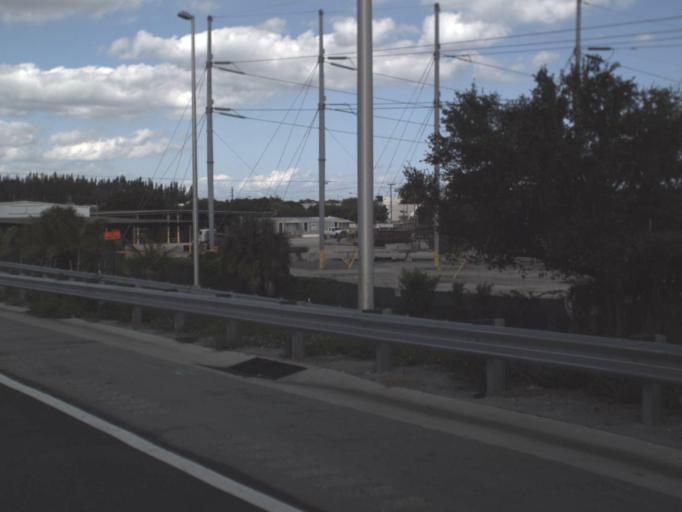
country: US
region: Florida
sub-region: Broward County
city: Davie
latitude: 26.0684
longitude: -80.2154
